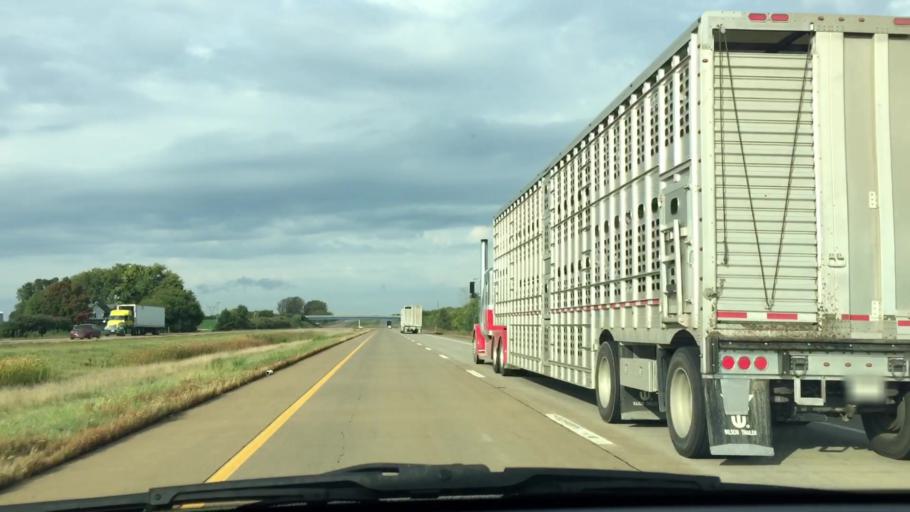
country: US
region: Illinois
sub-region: Whiteside County
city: Sterling
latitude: 41.7656
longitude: -89.8173
